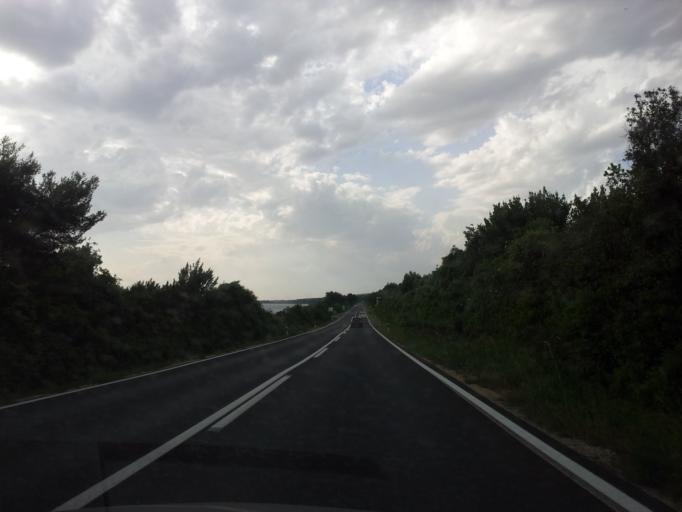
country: HR
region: Zadarska
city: Sukosan
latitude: 44.0217
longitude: 15.3540
